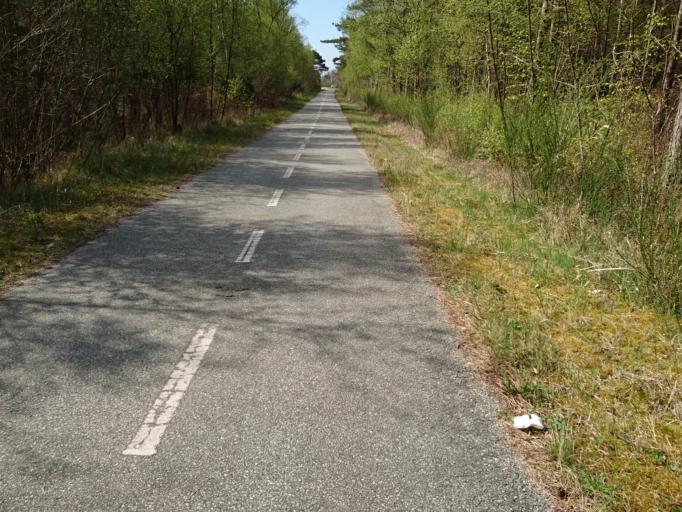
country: DK
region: North Denmark
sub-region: Frederikshavn Kommune
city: Skagen
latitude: 57.6419
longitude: 10.4615
